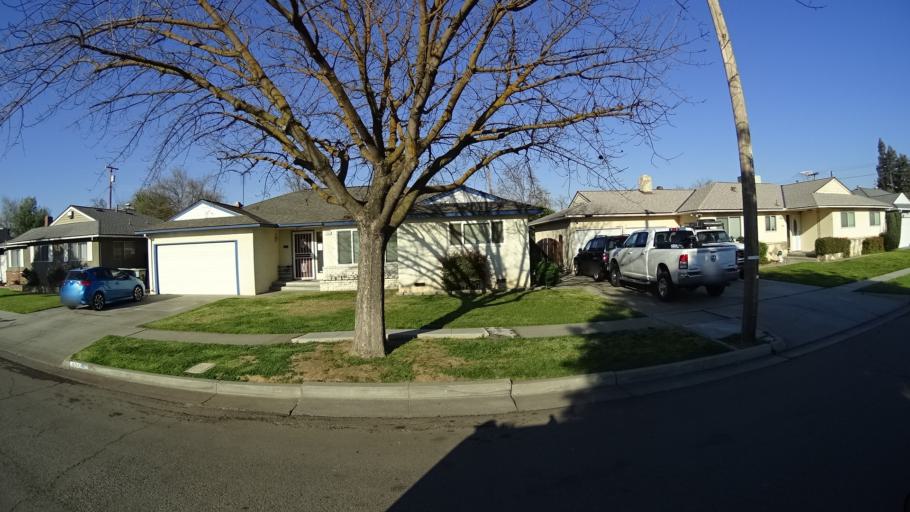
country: US
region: California
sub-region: Fresno County
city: Clovis
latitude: 36.8221
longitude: -119.7743
